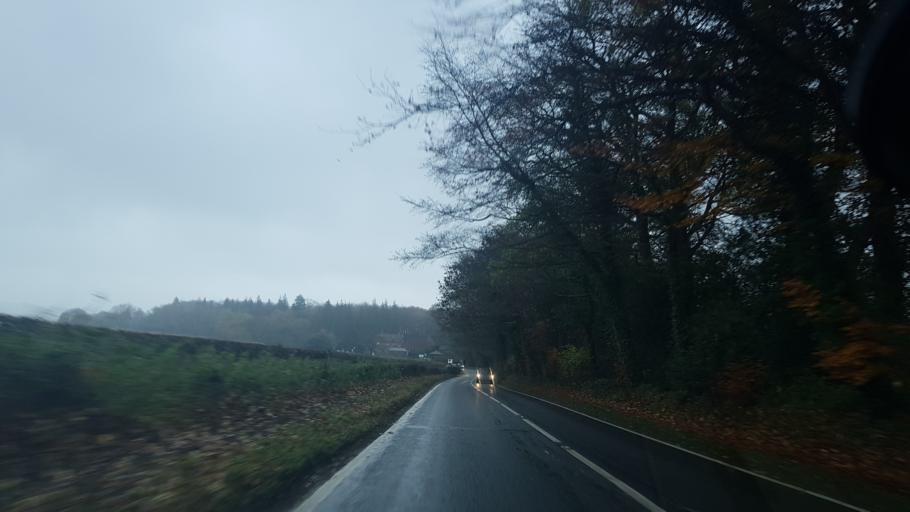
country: GB
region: England
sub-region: Surrey
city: Dorking
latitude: 51.2157
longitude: -0.3936
